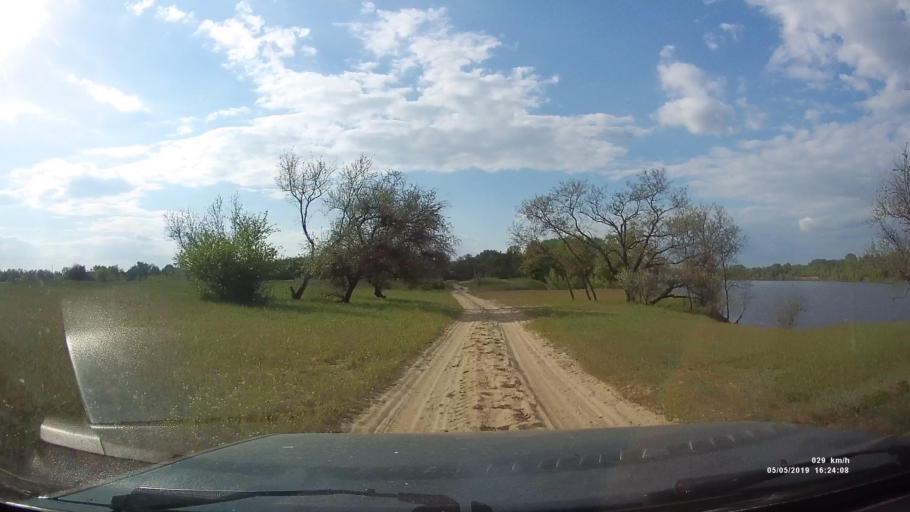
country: RU
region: Rostov
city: Konstantinovsk
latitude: 47.7584
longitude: 41.0273
